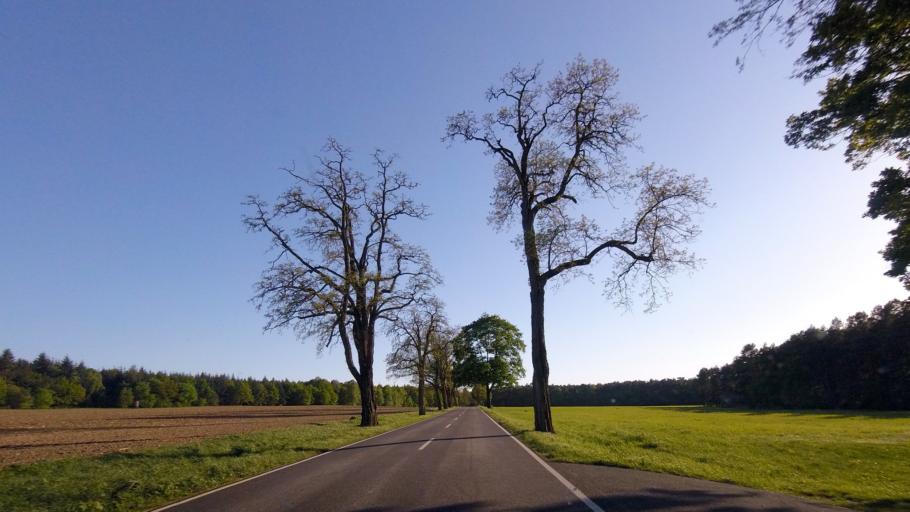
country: DE
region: Brandenburg
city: Baruth
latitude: 52.0100
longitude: 13.4465
